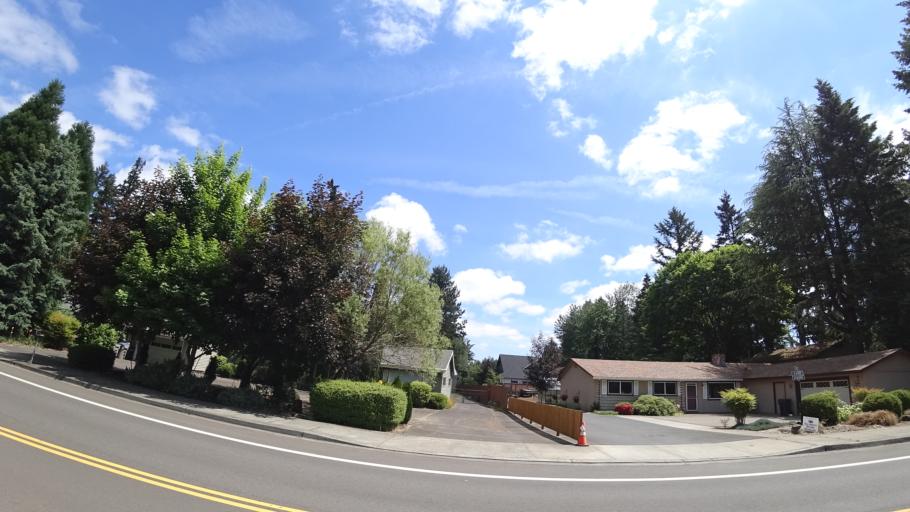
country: US
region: Oregon
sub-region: Washington County
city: King City
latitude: 45.4289
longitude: -122.8001
